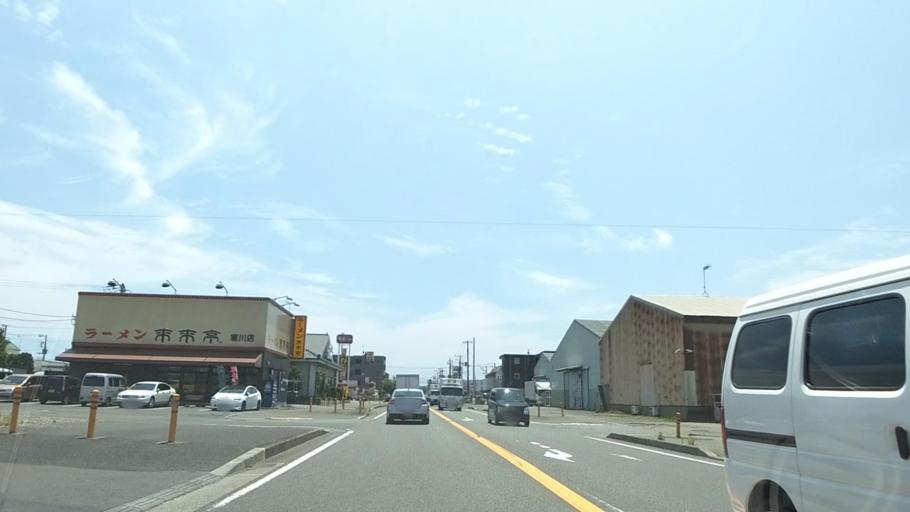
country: JP
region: Kanagawa
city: Atsugi
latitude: 35.3983
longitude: 139.3812
